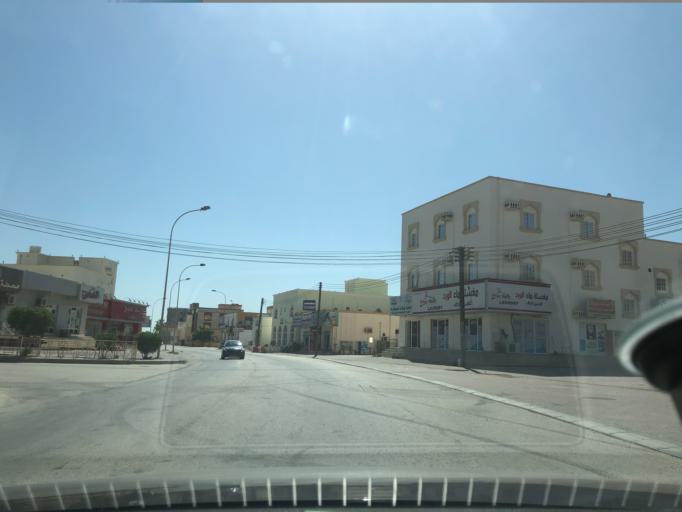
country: OM
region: Zufar
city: Salalah
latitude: 17.0219
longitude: 54.1564
